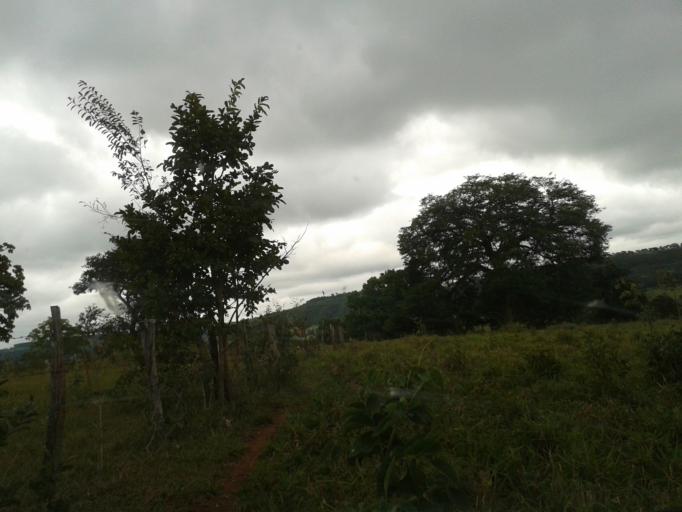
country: BR
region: Minas Gerais
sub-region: Campina Verde
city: Campina Verde
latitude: -19.4683
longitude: -49.6111
